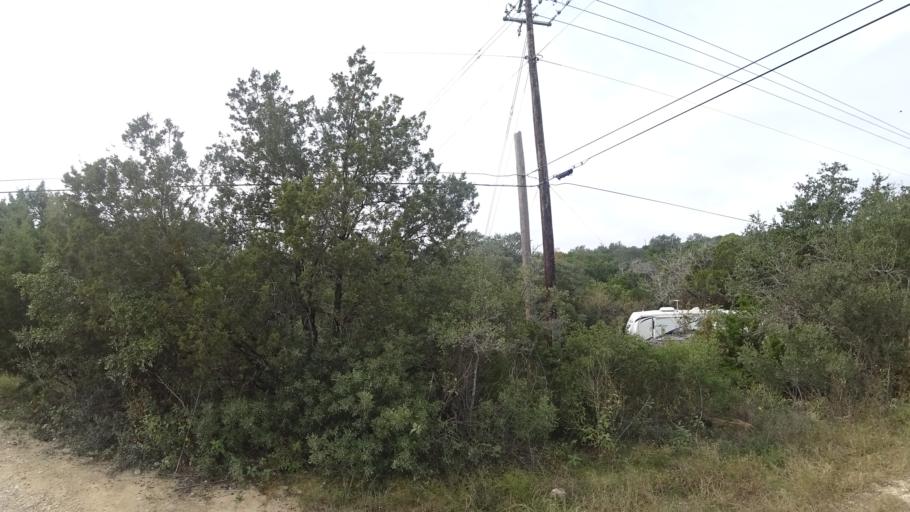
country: US
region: Texas
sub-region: Travis County
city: Hudson Bend
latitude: 30.3939
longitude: -97.9284
